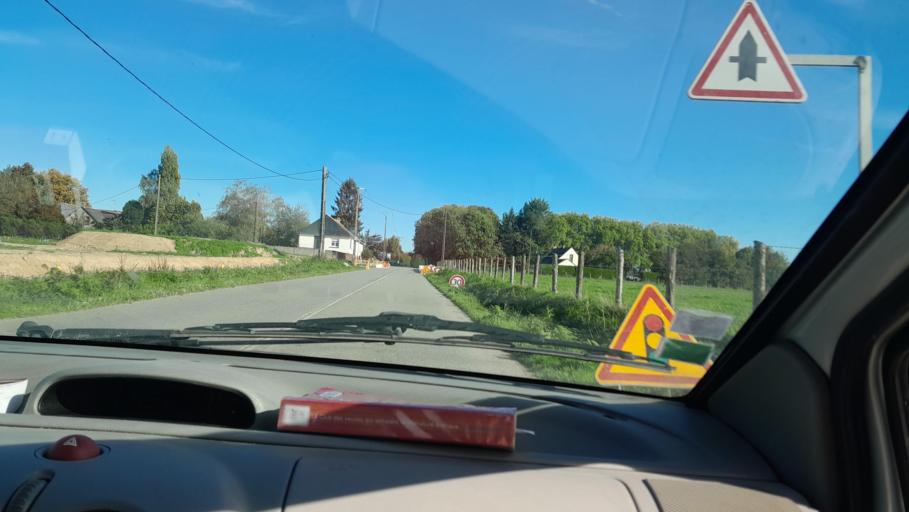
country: FR
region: Brittany
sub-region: Departement d'Ille-et-Vilaine
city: Etrelles
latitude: 48.0569
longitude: -1.1826
